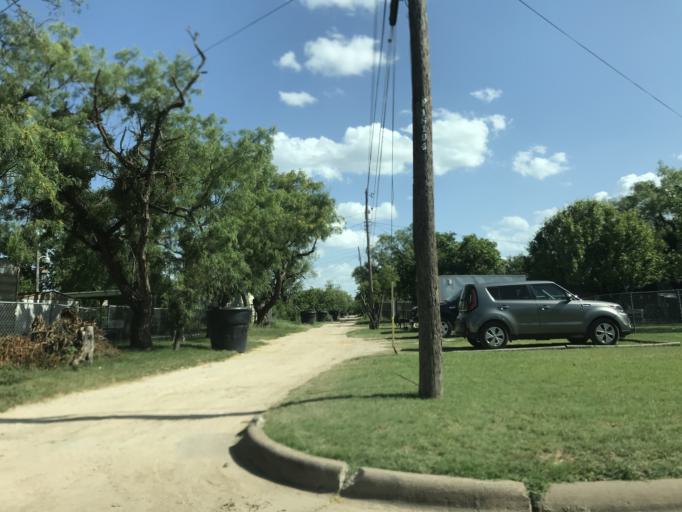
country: US
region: Texas
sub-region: Taylor County
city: Abilene
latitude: 32.4297
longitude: -99.7589
